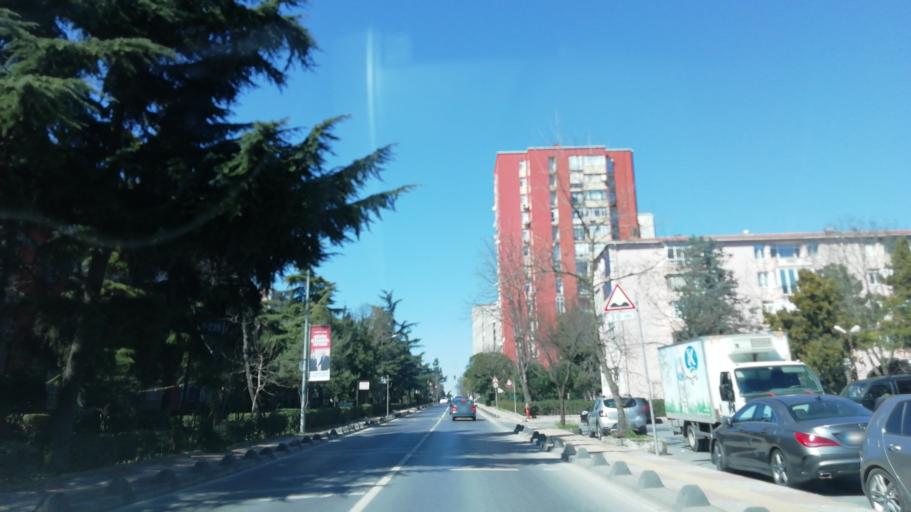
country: TR
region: Istanbul
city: Bahcelievler
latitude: 40.9834
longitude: 28.8641
